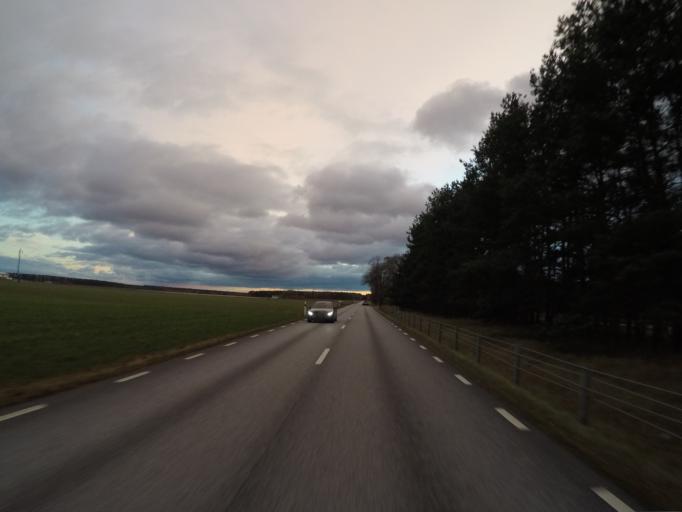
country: SE
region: Skane
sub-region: Kristianstads Kommun
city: Norra Asum
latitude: 55.9278
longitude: 14.0746
